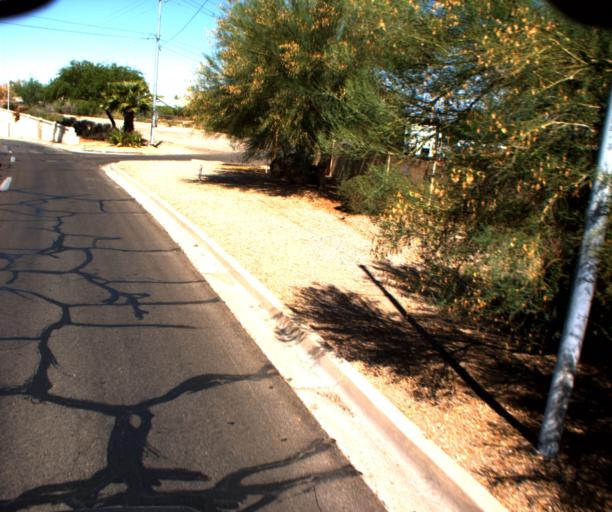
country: US
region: Arizona
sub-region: Pinal County
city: Casa Grande
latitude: 32.8804
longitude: -111.7605
